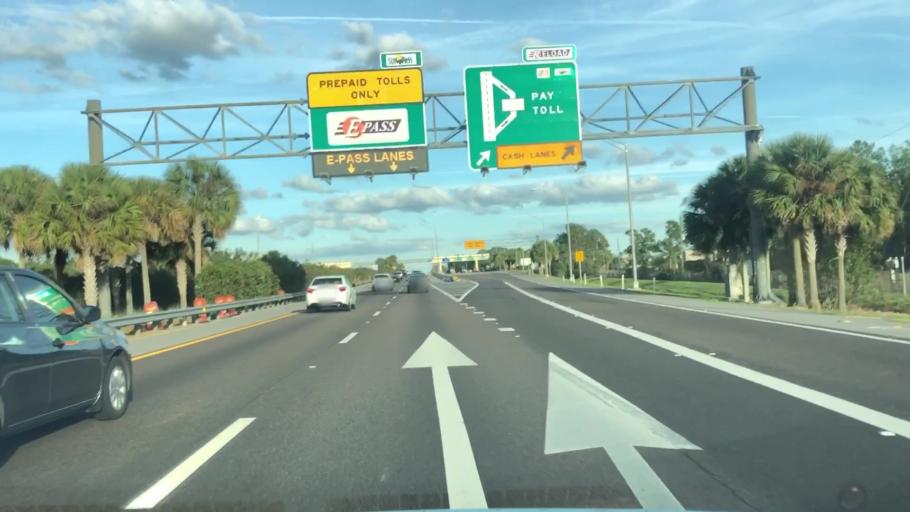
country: US
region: Florida
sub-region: Orange County
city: Hunters Creek
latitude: 28.3546
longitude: -81.4634
